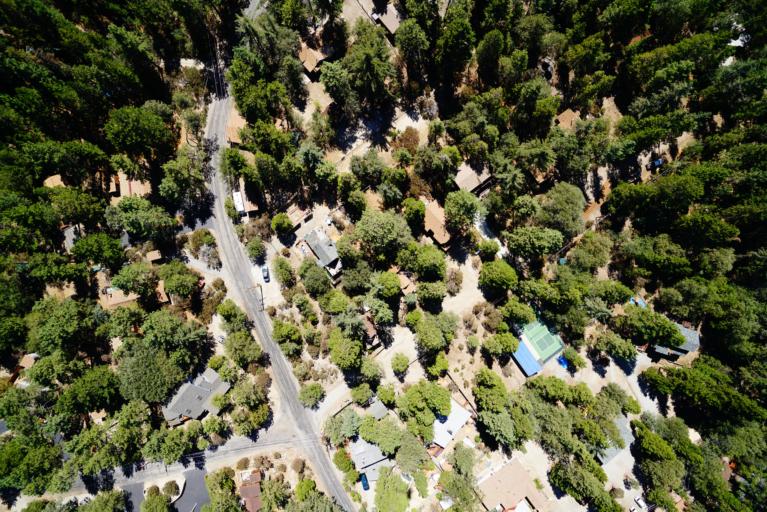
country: US
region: California
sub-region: Riverside County
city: Idyllwild-Pine Cove
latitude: 33.7552
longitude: -116.7409
